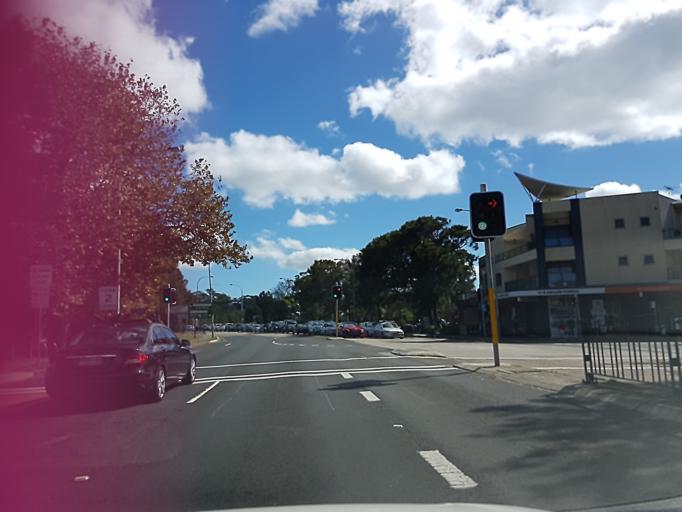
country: AU
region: New South Wales
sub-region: Warringah
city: Narrabeen
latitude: -33.7130
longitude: 151.2972
